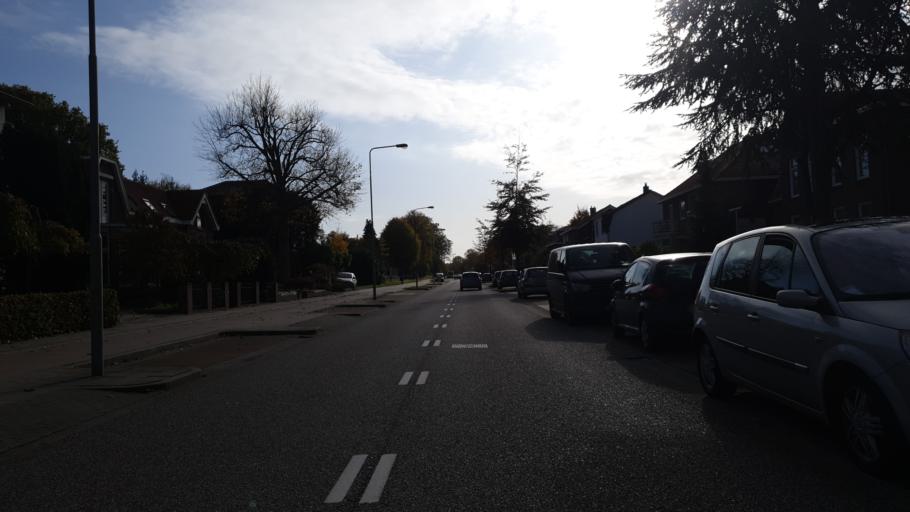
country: NL
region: Limburg
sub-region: Gemeente Gennep
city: Gennep
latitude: 51.6924
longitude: 5.9730
